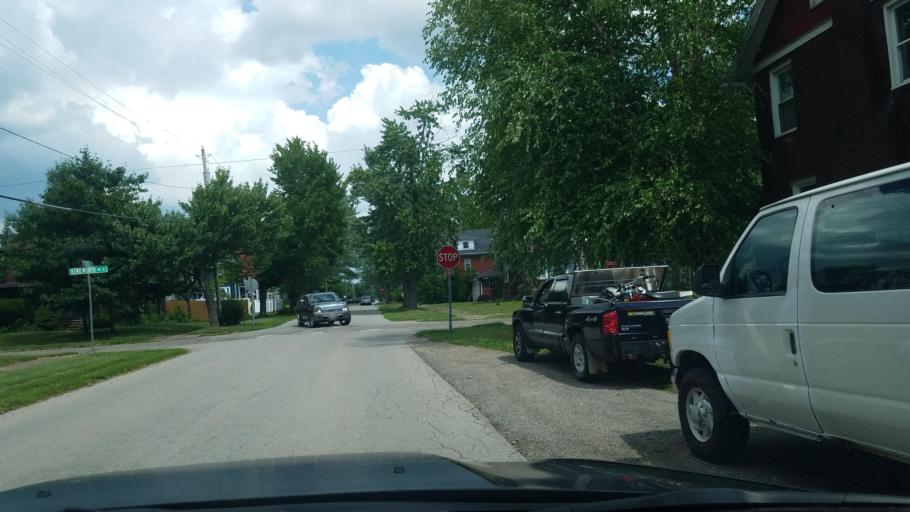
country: US
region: Ohio
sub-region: Trumbull County
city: Warren
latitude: 41.2343
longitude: -80.7960
